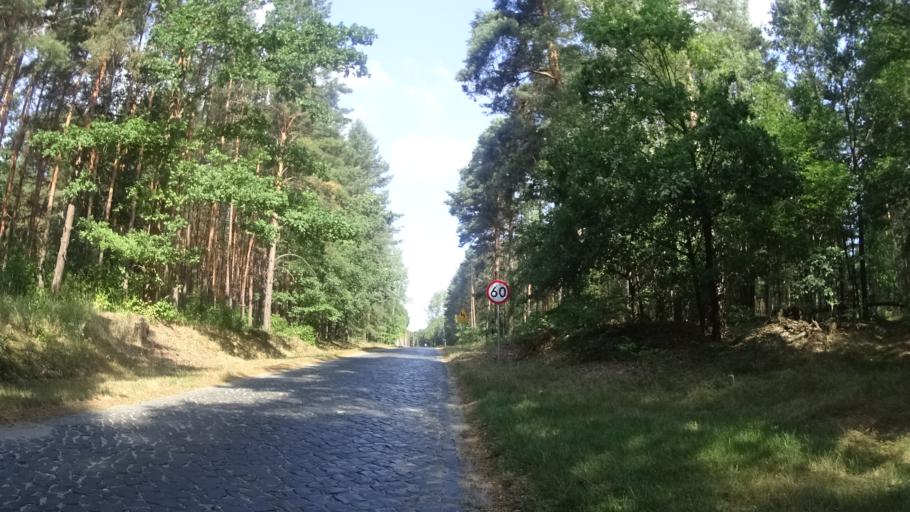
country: PL
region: Lubusz
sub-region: Powiat zarski
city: Leknica
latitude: 51.5082
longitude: 14.8373
